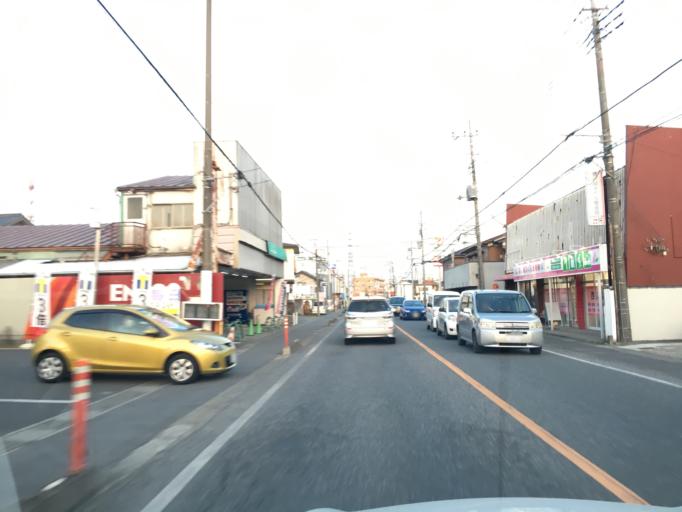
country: JP
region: Saitama
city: Kawagoe
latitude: 35.9188
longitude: 139.4595
